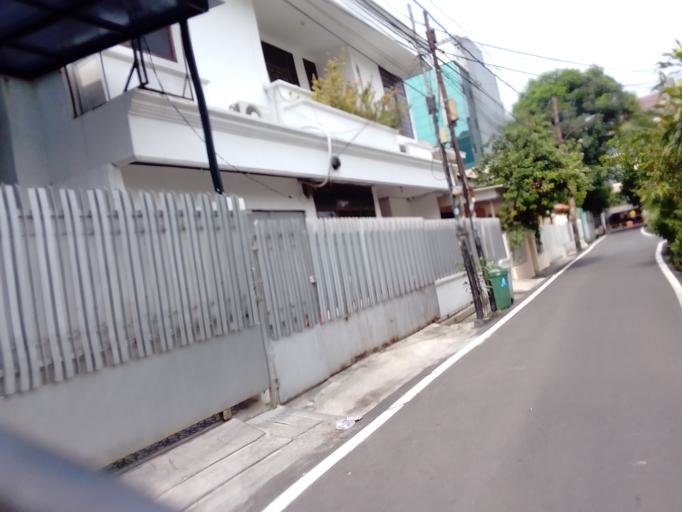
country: ID
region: Jakarta Raya
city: Jakarta
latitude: -6.1747
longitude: 106.8111
